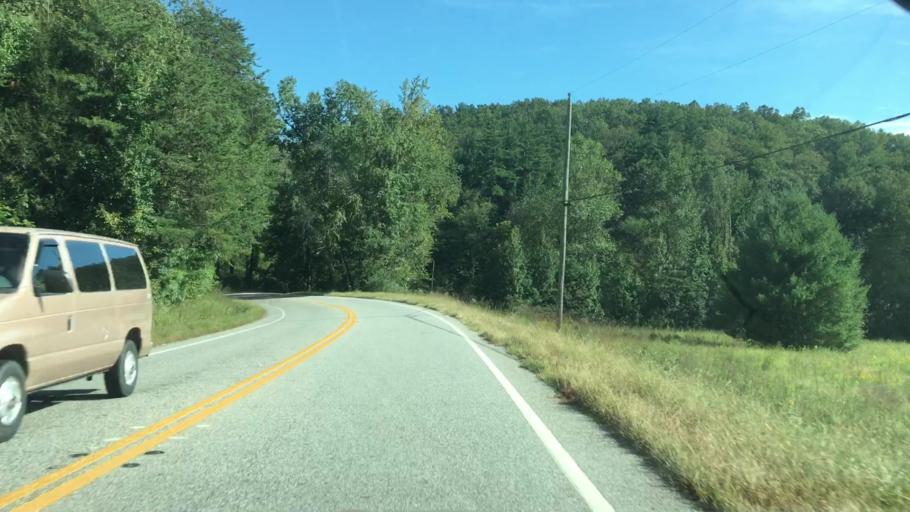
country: US
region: Georgia
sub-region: White County
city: Cleveland
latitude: 34.6615
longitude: -83.8992
